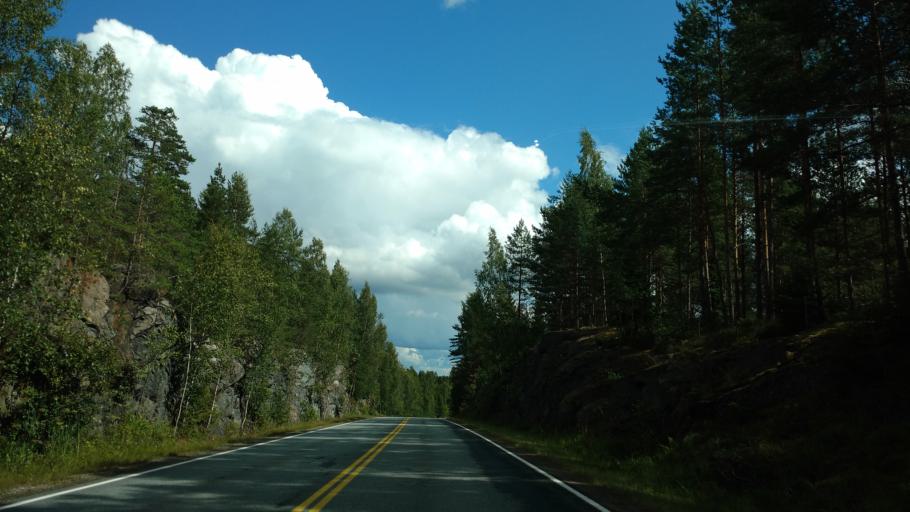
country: FI
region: Varsinais-Suomi
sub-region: Salo
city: Kisko
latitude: 60.2338
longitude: 23.5959
